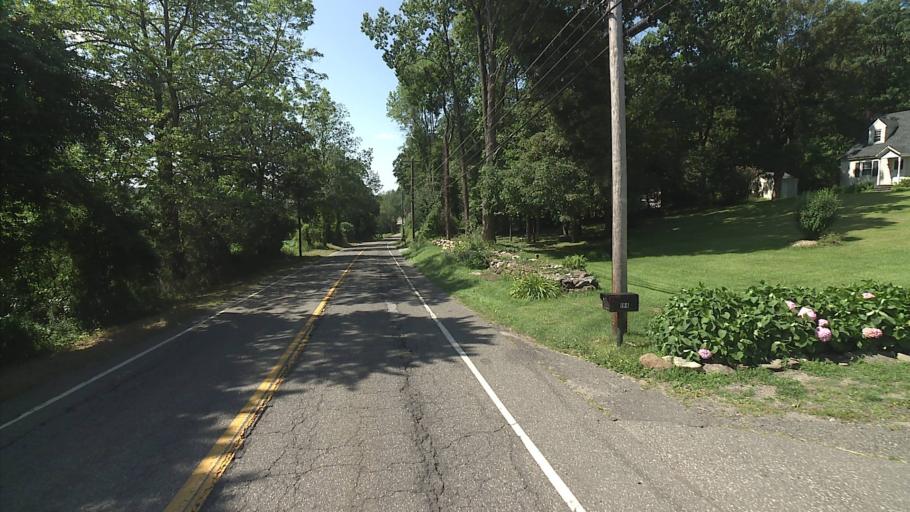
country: US
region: Connecticut
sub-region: Litchfield County
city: New Preston
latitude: 41.7230
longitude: -73.3418
